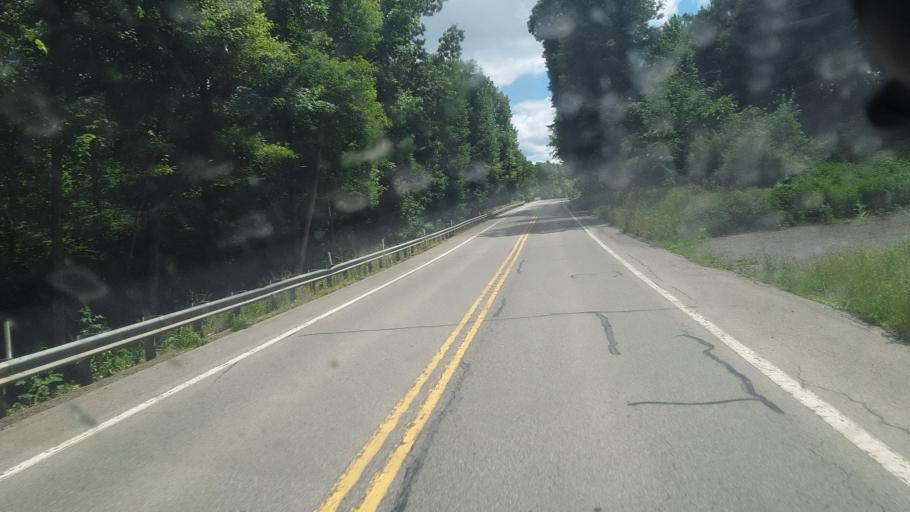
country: US
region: Pennsylvania
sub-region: Butler County
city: Slippery Rock
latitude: 41.0057
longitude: -80.1739
